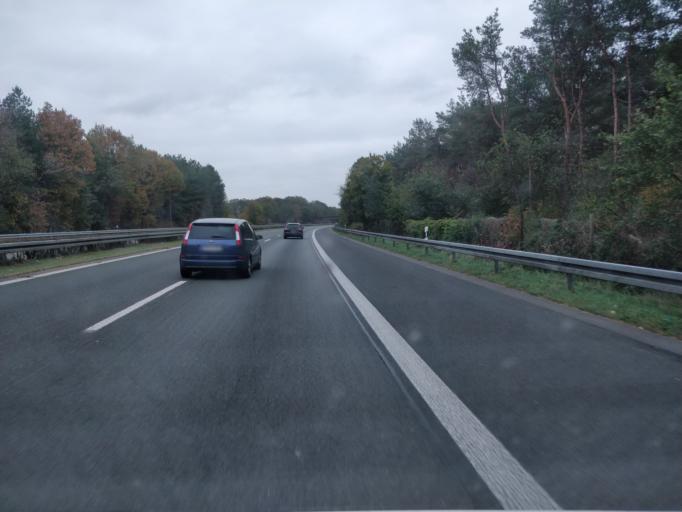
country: DE
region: North Rhine-Westphalia
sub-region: Regierungsbezirk Munster
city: Isselburg
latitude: 51.8012
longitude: 6.4872
